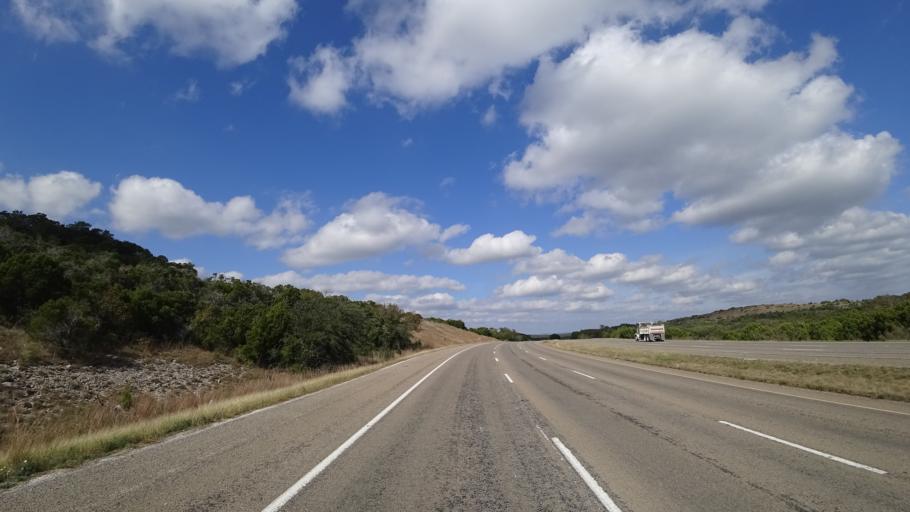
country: US
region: Texas
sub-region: Travis County
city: Barton Creek
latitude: 30.2706
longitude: -97.8963
